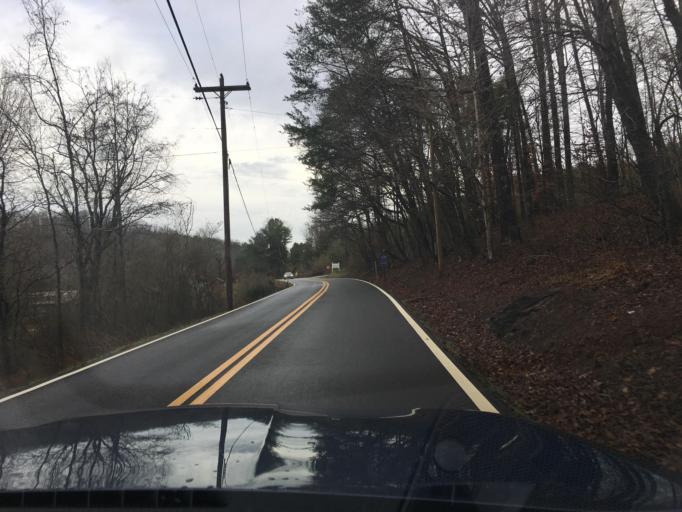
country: US
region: Tennessee
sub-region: McMinn County
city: Englewood
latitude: 35.3843
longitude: -84.4385
